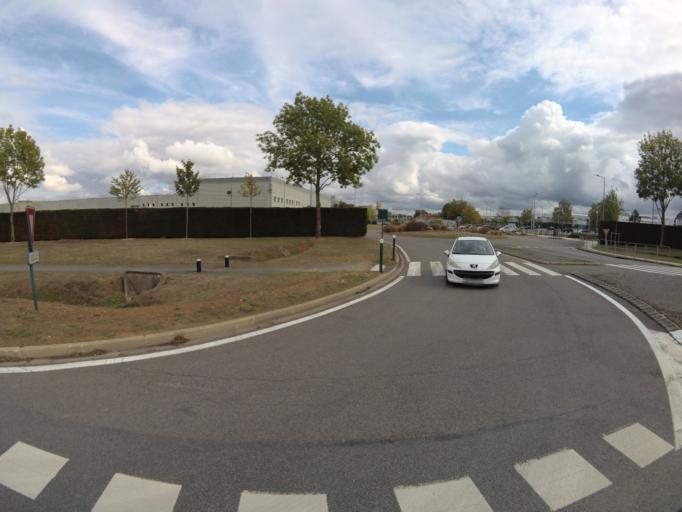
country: FR
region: Ile-de-France
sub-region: Departement de Seine-et-Marne
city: Montevrain
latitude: 48.8665
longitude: 2.7655
